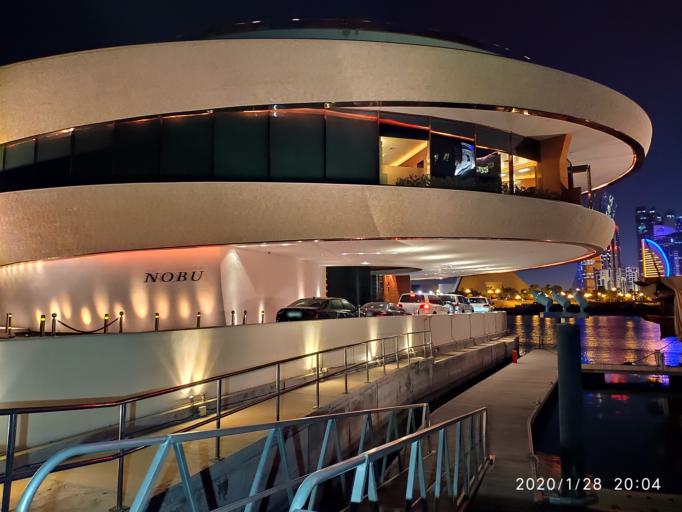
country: QA
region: Baladiyat ad Dawhah
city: Doha
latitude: 25.3236
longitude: 51.5412
